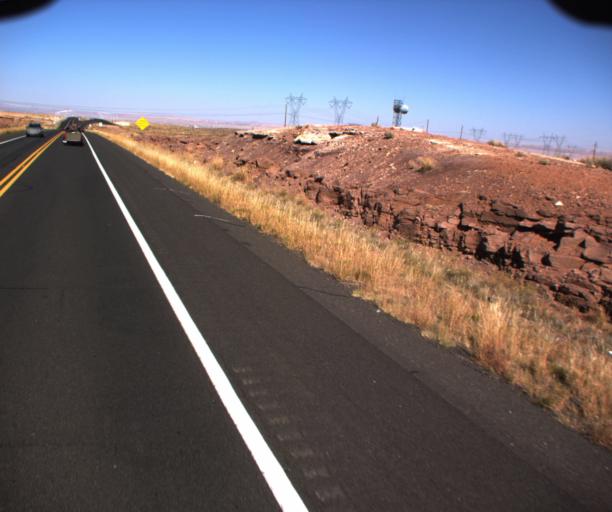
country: US
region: Arizona
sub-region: Coconino County
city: Tuba City
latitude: 35.8300
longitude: -111.4384
